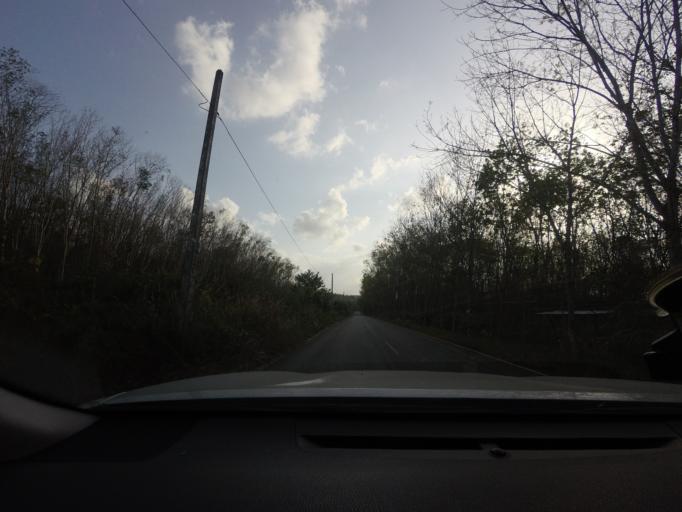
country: TH
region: Pattani
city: Mae Lan
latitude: 6.6191
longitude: 101.2471
